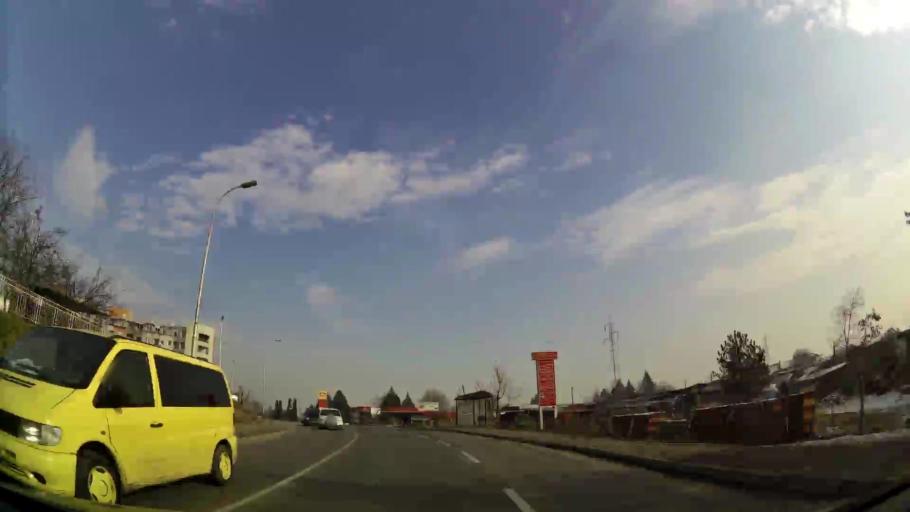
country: MK
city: Creshevo
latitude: 42.0047
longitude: 21.5006
